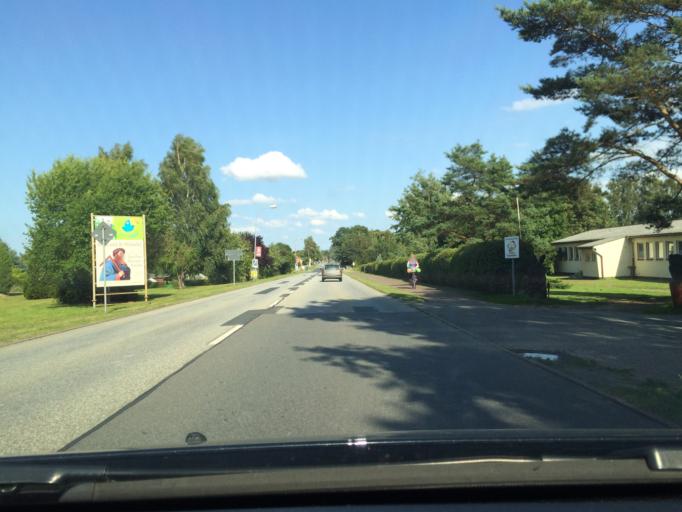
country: DE
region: Mecklenburg-Vorpommern
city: Barth
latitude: 54.2954
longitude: 12.7225
